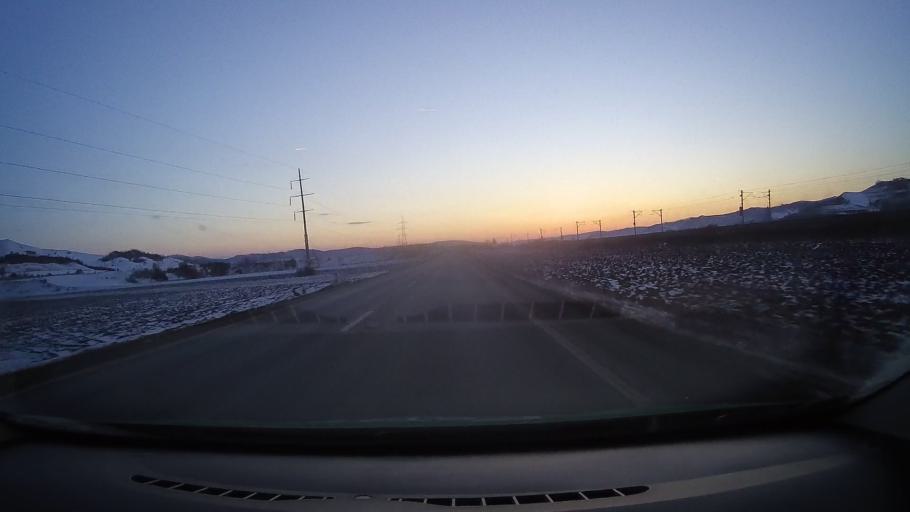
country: RO
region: Sibiu
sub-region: Comuna Alma
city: Alma
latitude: 46.1907
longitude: 24.4600
